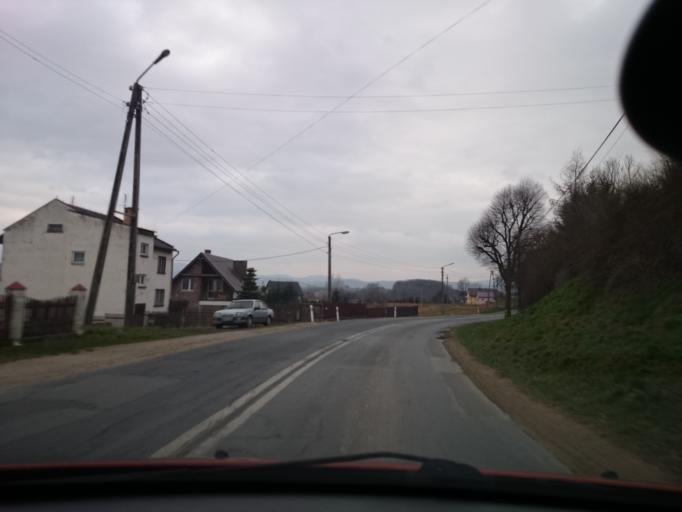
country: PL
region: Lower Silesian Voivodeship
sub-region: Powiat zabkowicki
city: Kamieniec Zabkowicki
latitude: 50.5215
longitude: 16.9026
